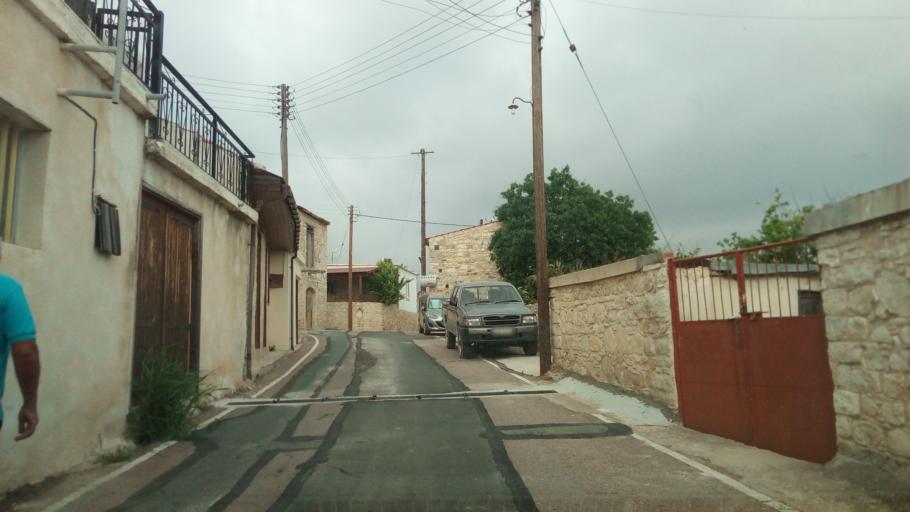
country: CY
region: Limassol
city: Pachna
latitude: 34.8487
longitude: 32.7068
